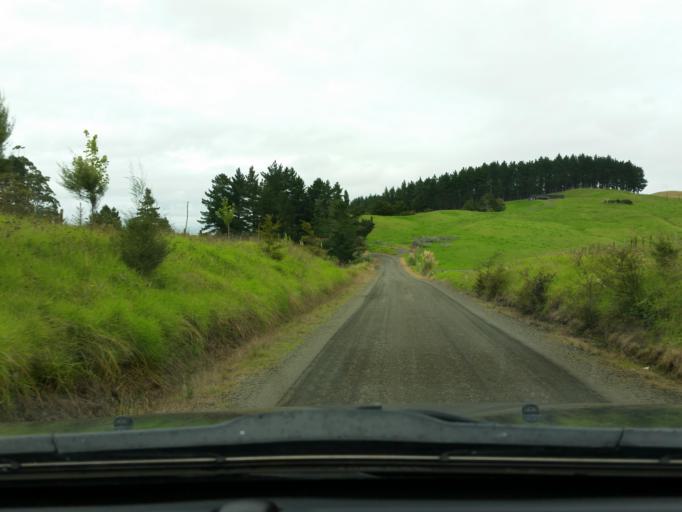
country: NZ
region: Northland
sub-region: Kaipara District
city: Dargaville
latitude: -35.8607
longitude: 174.0159
